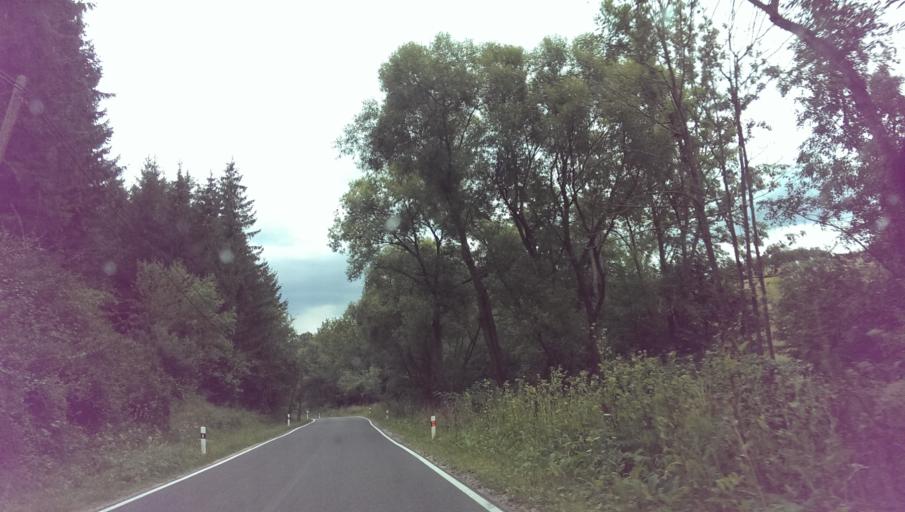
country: CZ
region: South Moravian
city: Velka nad Velickou
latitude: 48.8732
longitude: 17.5879
